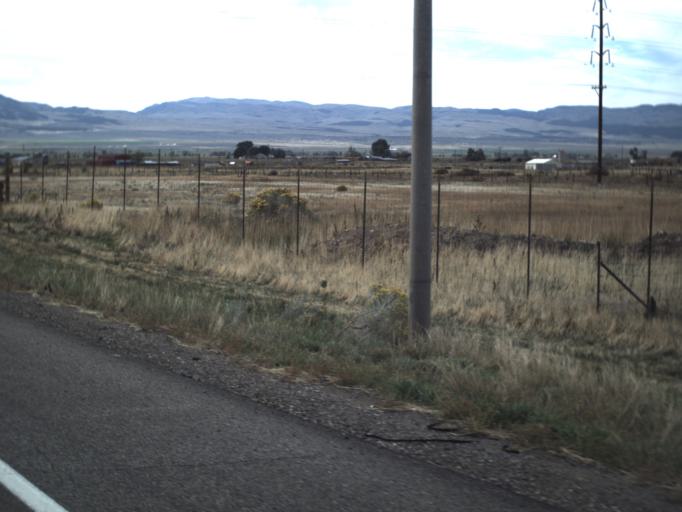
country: US
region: Utah
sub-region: Beaver County
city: Beaver
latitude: 38.2877
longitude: -112.6509
